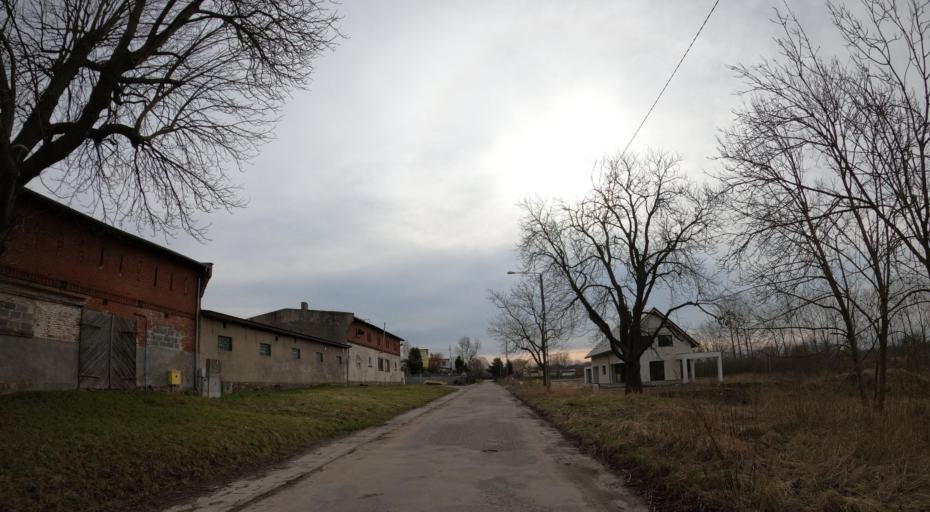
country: PL
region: West Pomeranian Voivodeship
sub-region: Powiat pyrzycki
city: Pyrzyce
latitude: 53.1348
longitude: 14.9079
